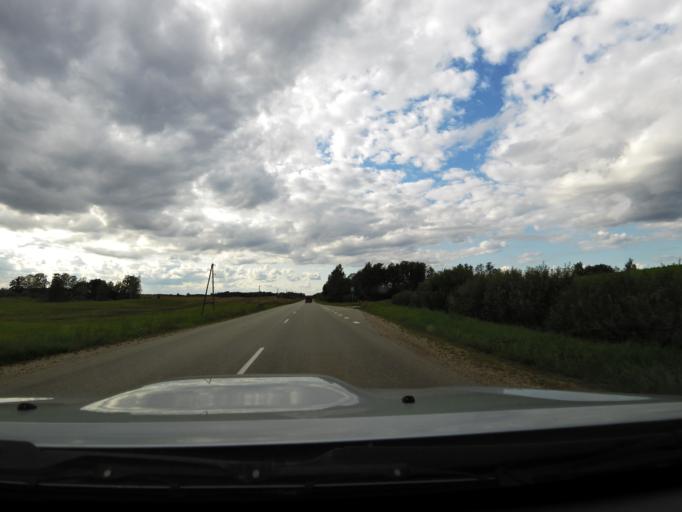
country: LV
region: Akniste
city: Akniste
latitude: 55.9858
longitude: 25.9874
